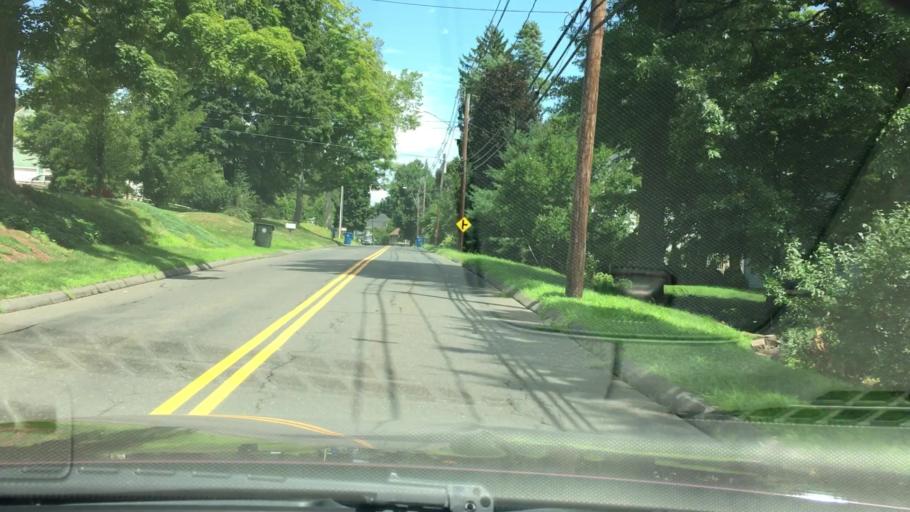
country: US
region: Connecticut
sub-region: Hartford County
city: Kensington
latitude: 41.6125
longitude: -72.7479
